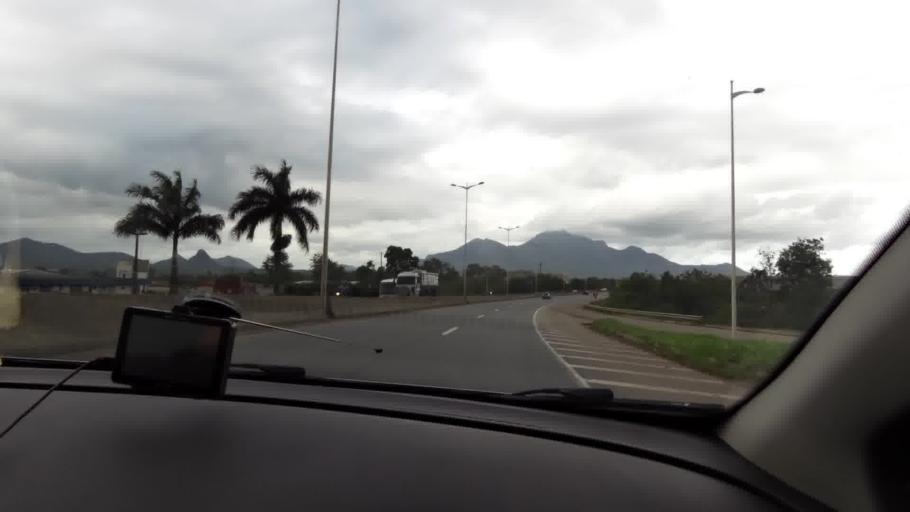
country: BR
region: Espirito Santo
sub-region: Vitoria
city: Vitoria
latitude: -20.2271
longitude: -40.3646
